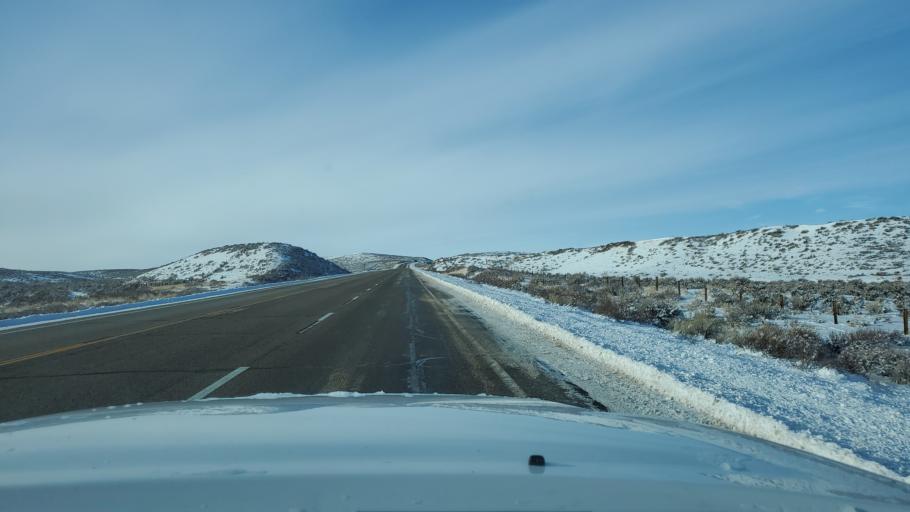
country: US
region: Colorado
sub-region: Rio Blanco County
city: Meeker
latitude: 40.5144
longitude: -108.1015
